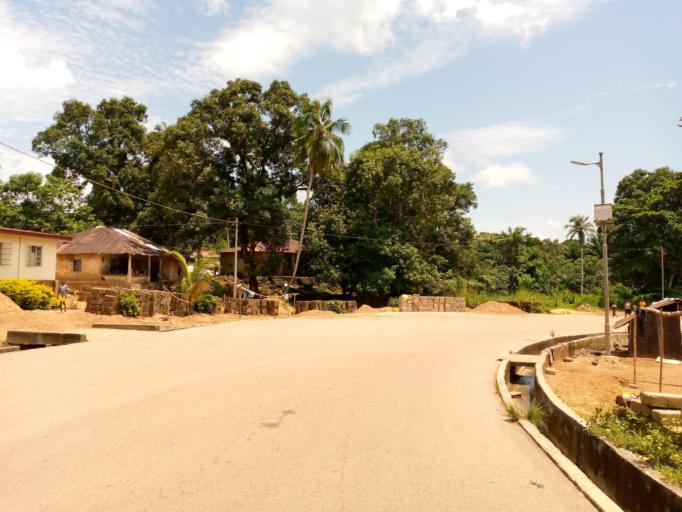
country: SL
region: Northern Province
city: Magburaka
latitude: 8.7246
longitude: -11.9523
